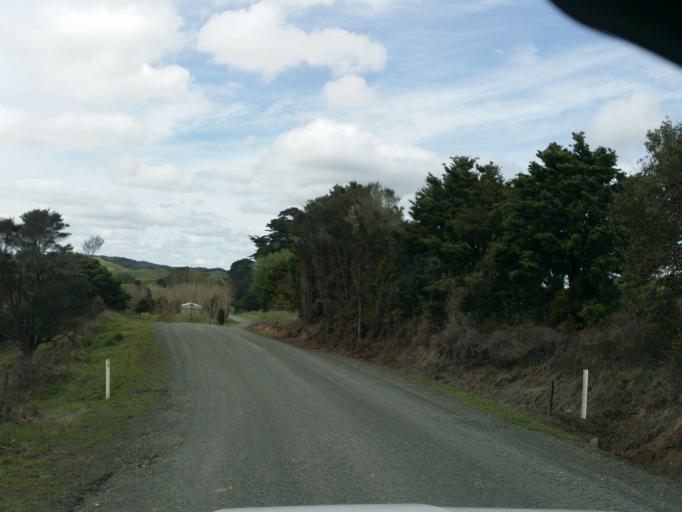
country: NZ
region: Northland
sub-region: Whangarei
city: Maungatapere
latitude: -35.9026
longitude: 174.1228
